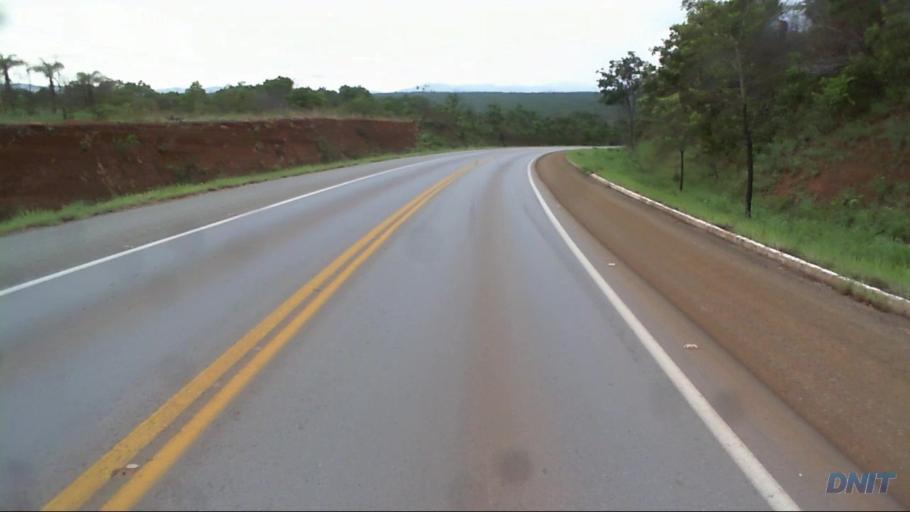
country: BR
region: Goias
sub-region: Uruacu
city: Uruacu
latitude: -14.7423
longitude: -49.0809
